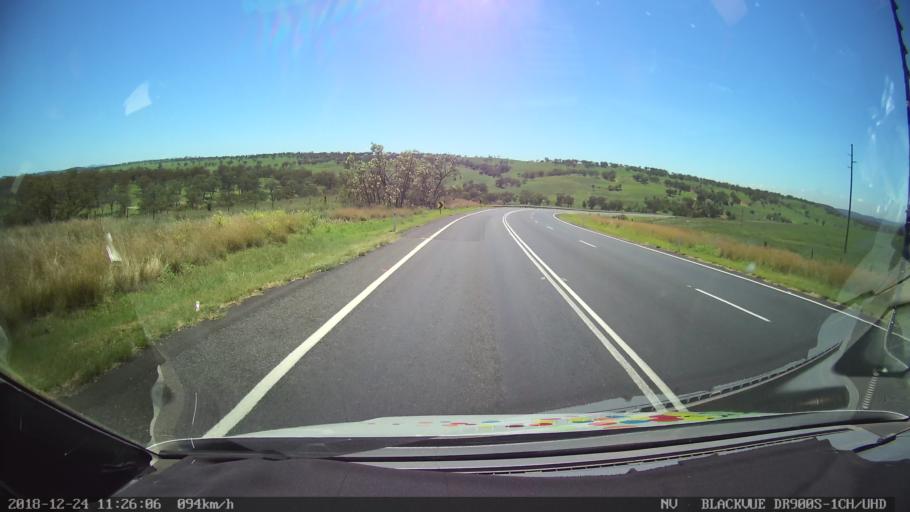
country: AU
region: New South Wales
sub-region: Upper Hunter Shire
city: Merriwa
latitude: -32.1680
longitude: 150.4264
